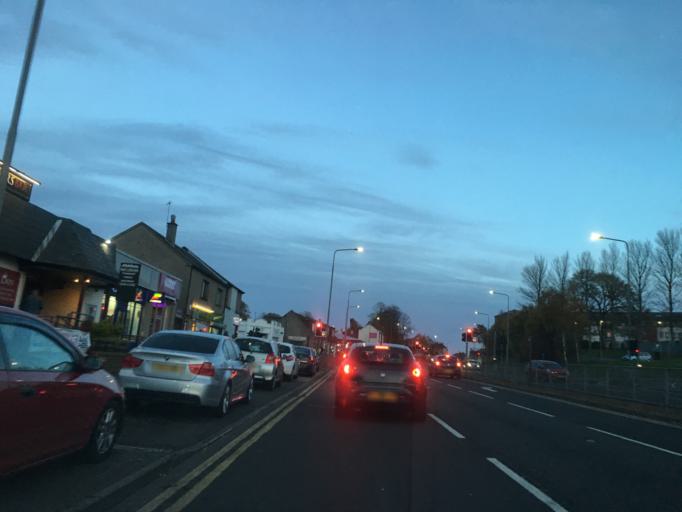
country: GB
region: Scotland
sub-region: Fife
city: Dunfermline
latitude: 56.0622
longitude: -3.4473
